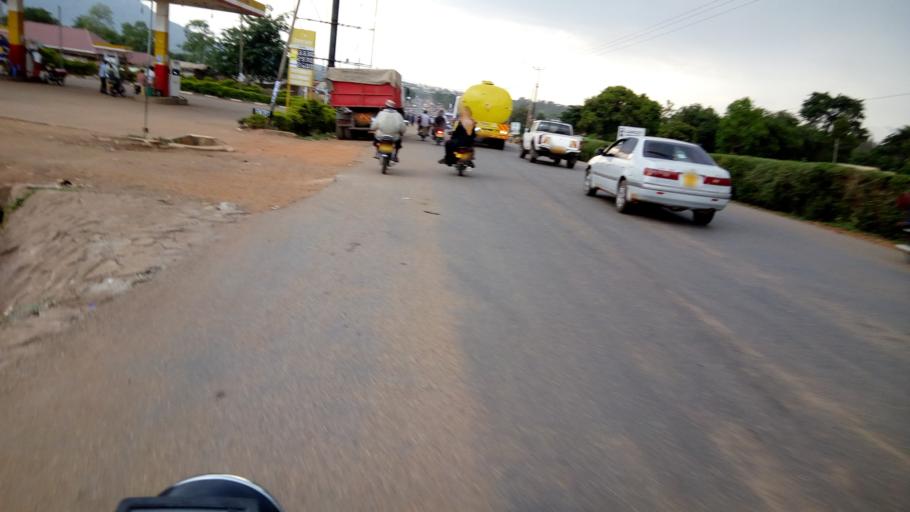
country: UG
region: Eastern Region
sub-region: Mbale District
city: Mbale
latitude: 1.0976
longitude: 34.1754
